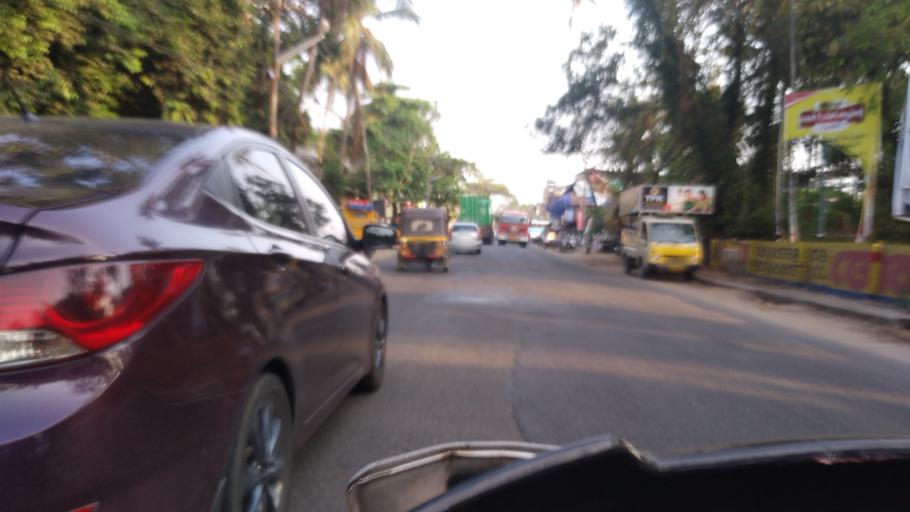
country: IN
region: Kerala
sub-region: Thrissur District
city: Thanniyam
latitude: 10.3757
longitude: 76.1232
